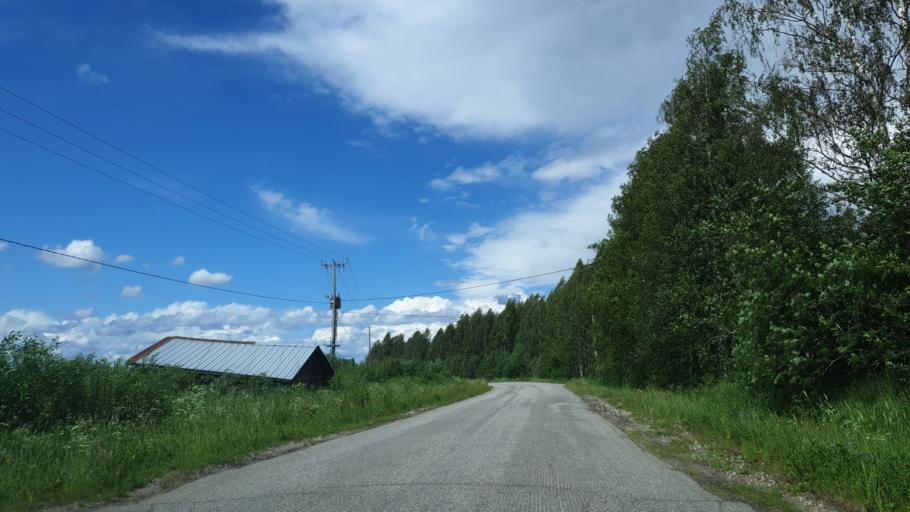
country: FI
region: Northern Savo
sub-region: Koillis-Savo
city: Kaavi
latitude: 62.9921
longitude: 28.7229
